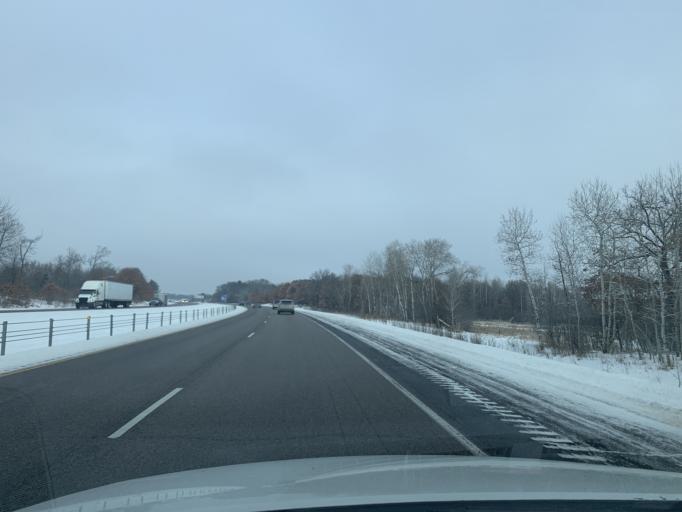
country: US
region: Minnesota
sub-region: Chisago County
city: Stacy
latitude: 45.3844
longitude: -92.9913
